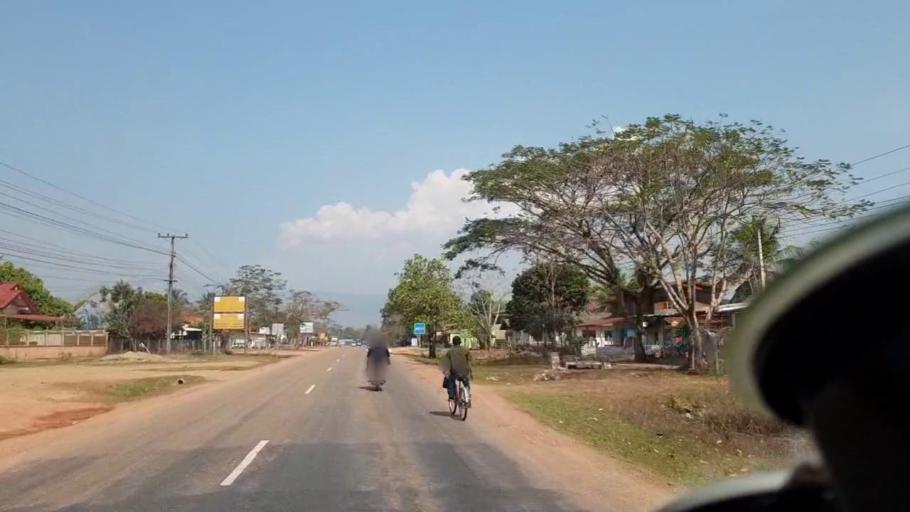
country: TH
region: Nong Khai
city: Rattanawapi
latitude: 18.1638
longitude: 103.0562
